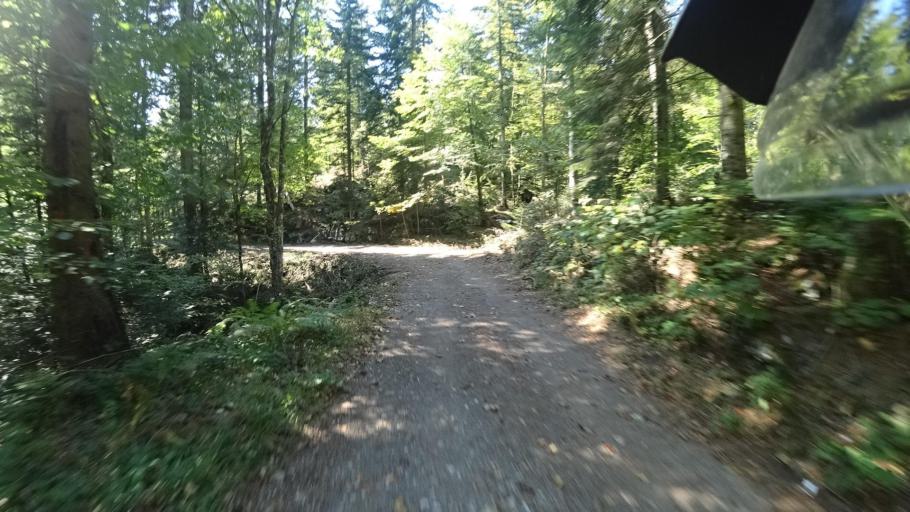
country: HR
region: Primorsko-Goranska
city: Vrbovsko
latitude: 45.2669
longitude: 15.1016
